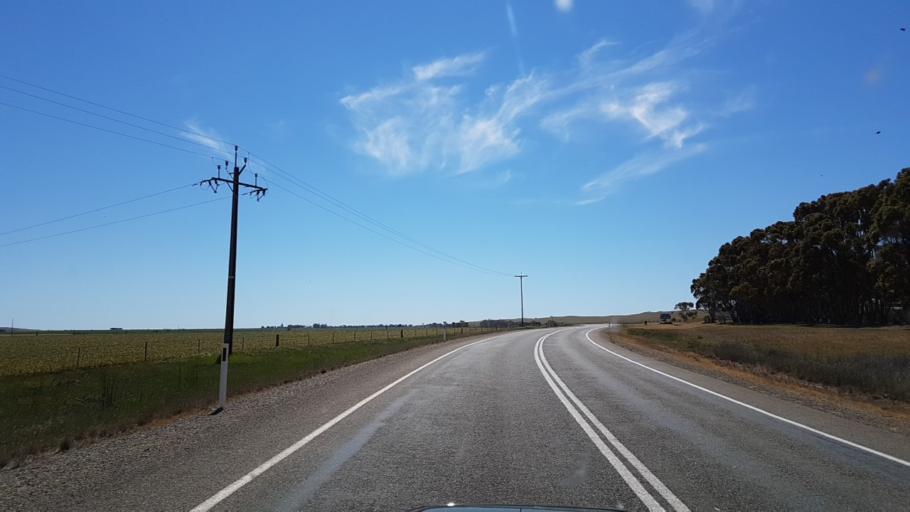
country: AU
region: South Australia
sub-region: Northern Areas
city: Jamestown
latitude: -33.4629
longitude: 138.8895
